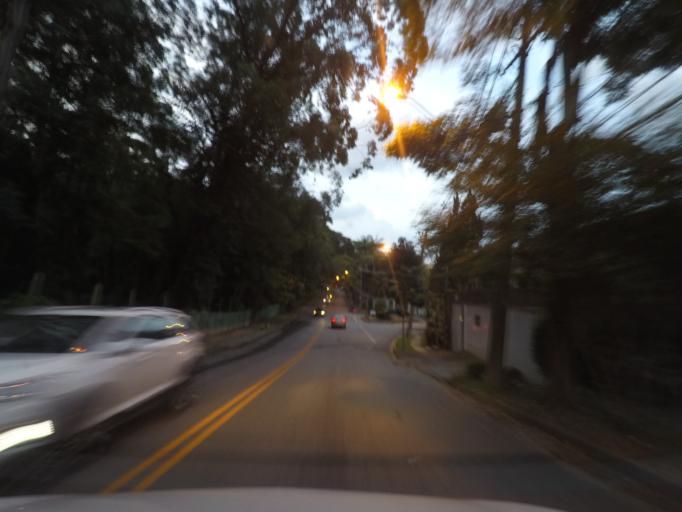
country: BR
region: Sao Paulo
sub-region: Taboao Da Serra
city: Taboao da Serra
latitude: -23.6058
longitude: -46.7092
